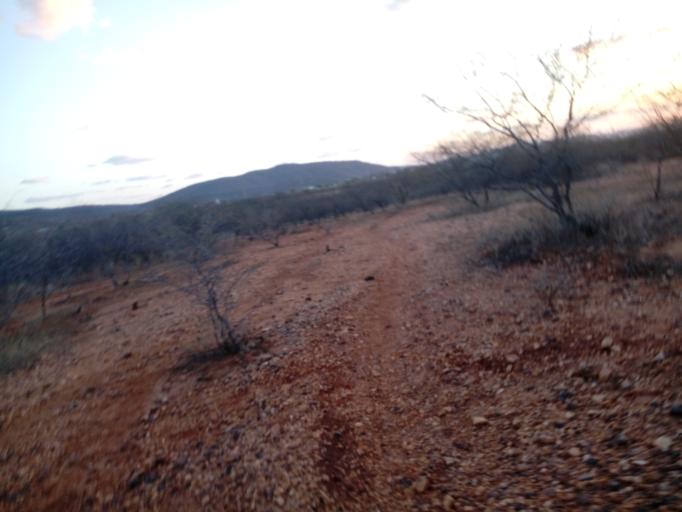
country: BR
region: Paraiba
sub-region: Patos
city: Patos
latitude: -6.8969
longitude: -37.5177
